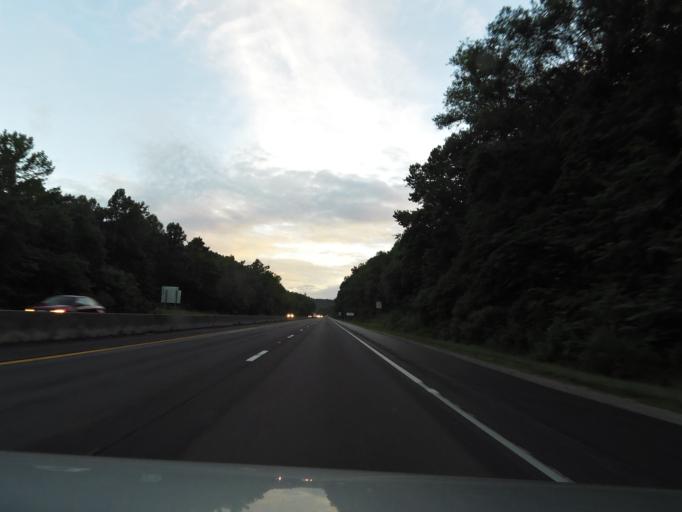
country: US
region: Tennessee
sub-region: Campbell County
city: Jellico
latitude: 36.5721
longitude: -84.1190
